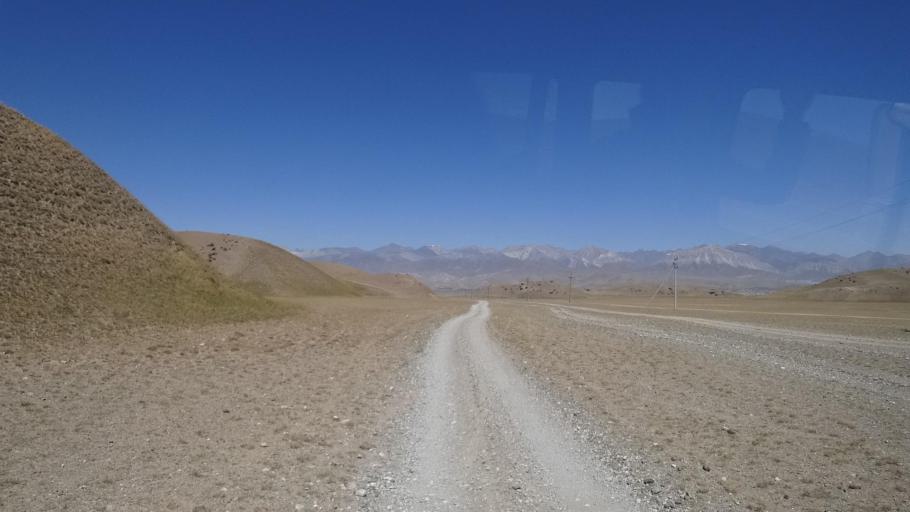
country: KG
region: Osh
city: Gul'cha
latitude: 39.6035
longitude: 72.8799
